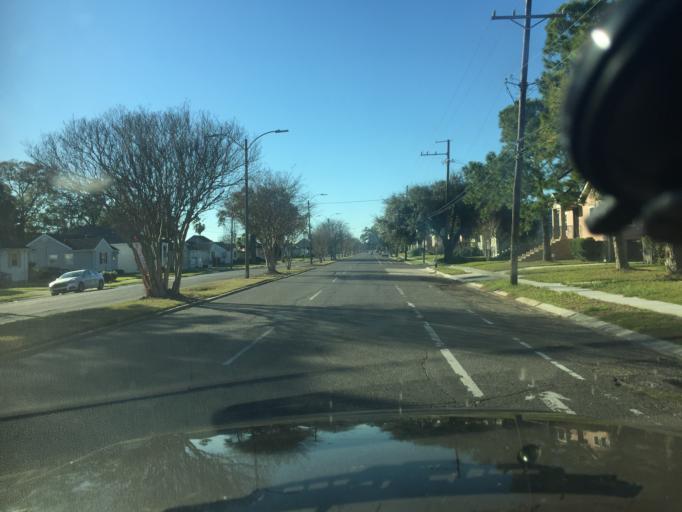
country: US
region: Louisiana
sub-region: Orleans Parish
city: New Orleans
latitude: 29.9889
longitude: -90.0801
